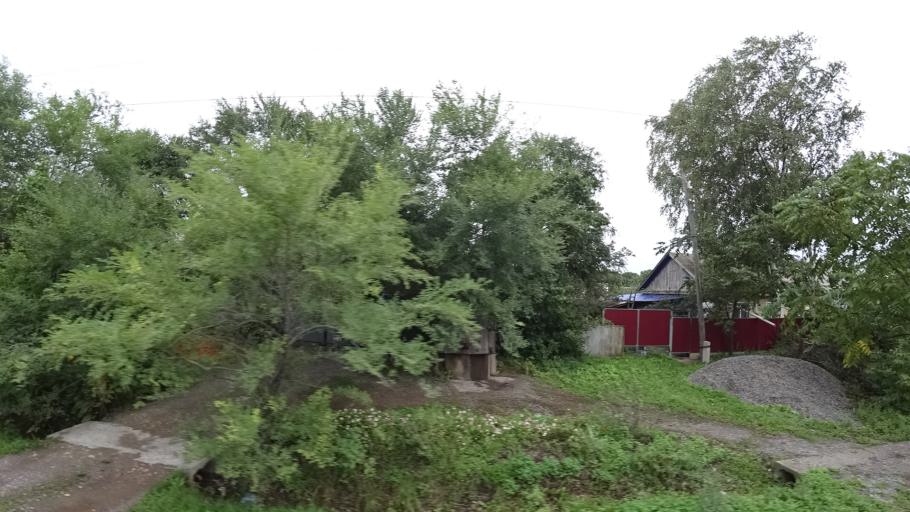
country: RU
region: Primorskiy
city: Chernigovka
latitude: 44.3373
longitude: 132.5930
